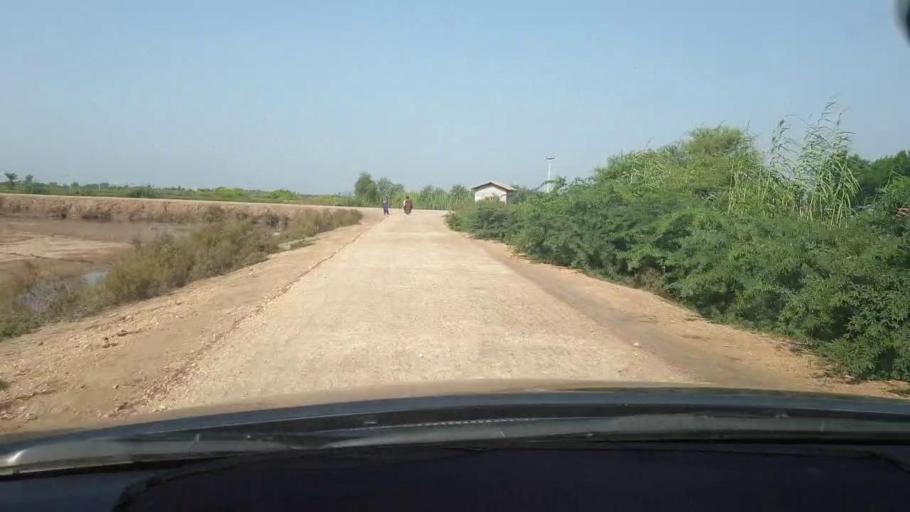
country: PK
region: Sindh
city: Tando Bago
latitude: 24.6800
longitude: 69.1287
